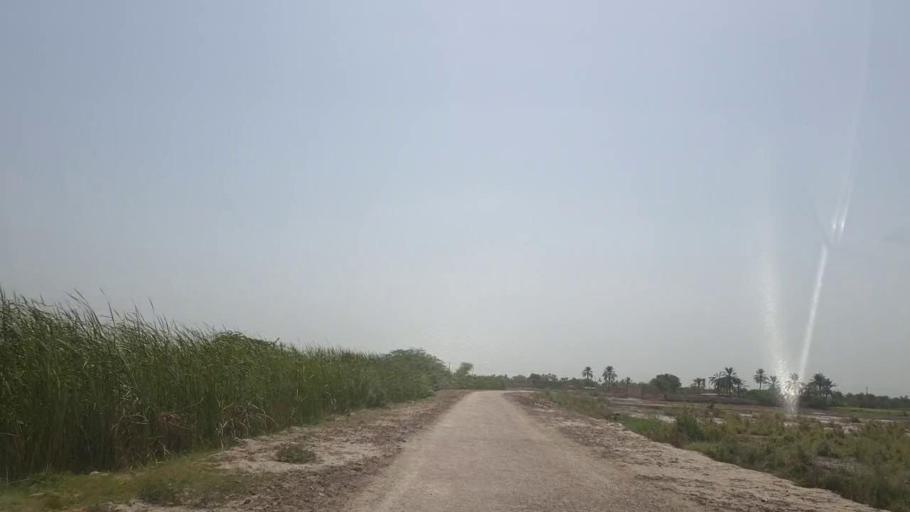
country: PK
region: Sindh
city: Gambat
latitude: 27.3128
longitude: 68.5438
